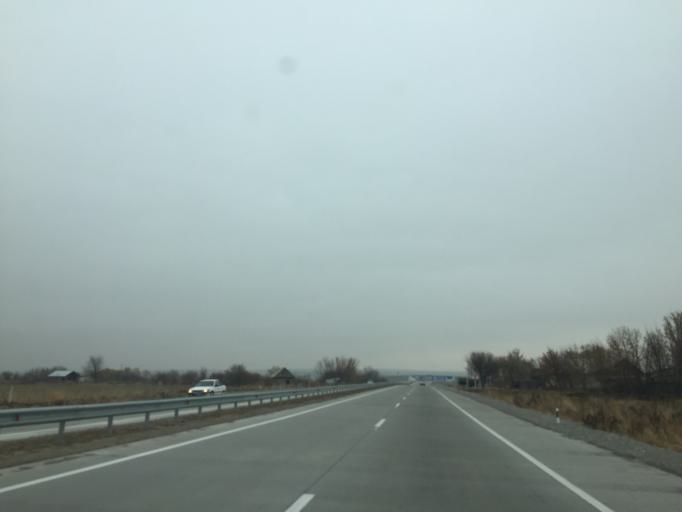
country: KZ
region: Ongtustik Qazaqstan
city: Aksu
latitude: 42.4710
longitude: 69.8043
